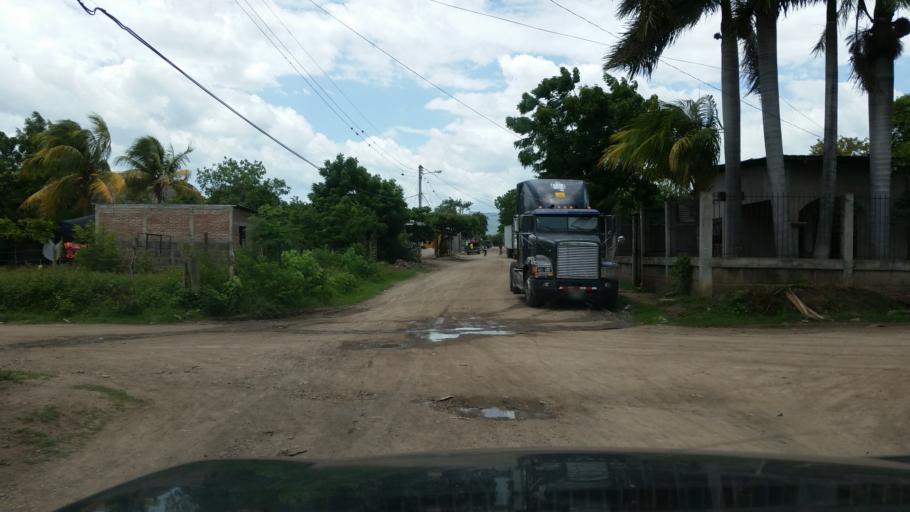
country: NI
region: Matagalpa
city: Ciudad Dario
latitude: 12.8607
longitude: -86.0911
